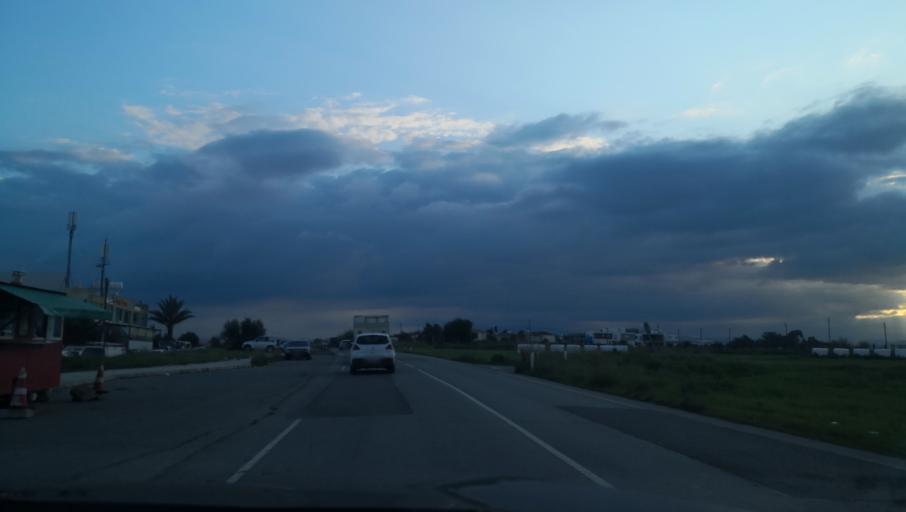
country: CY
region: Lefkosia
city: Tseri
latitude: 35.1021
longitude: 33.3282
